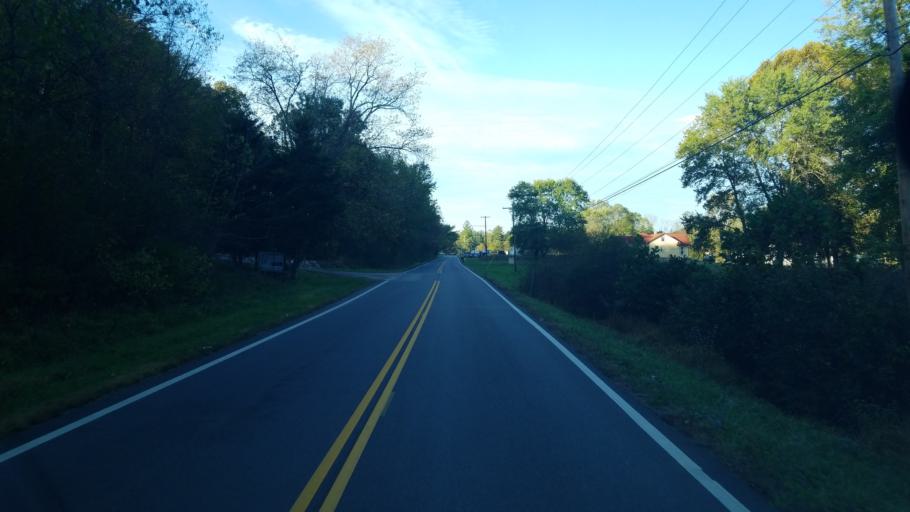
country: US
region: Ohio
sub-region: Jackson County
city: Wellston
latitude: 39.1350
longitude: -82.5244
